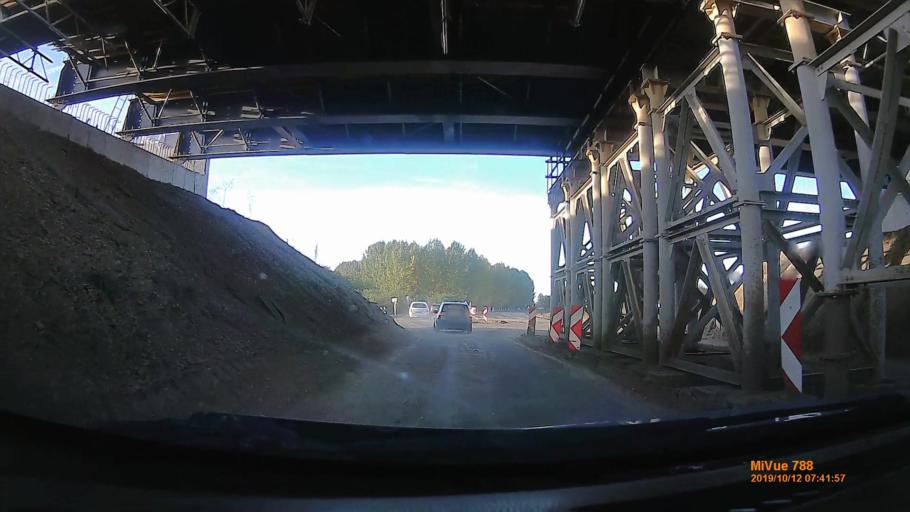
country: HU
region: Hajdu-Bihar
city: Pocsaj
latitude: 47.2041
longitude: 21.7956
